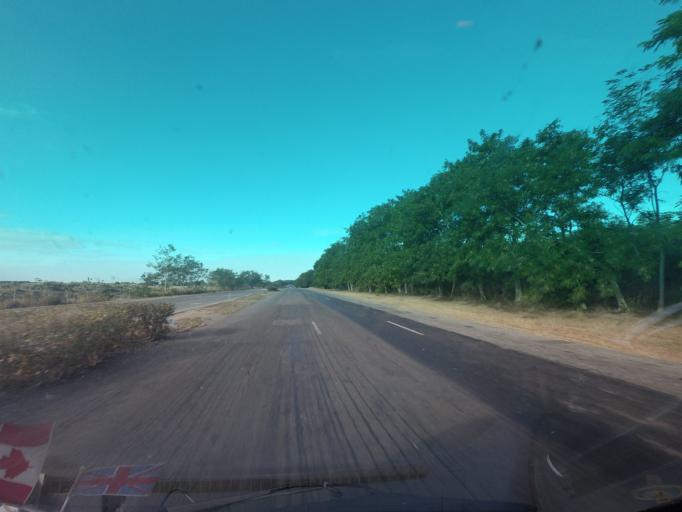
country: CU
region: Cienfuegos
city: Rodas
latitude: 22.4420
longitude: -80.5047
